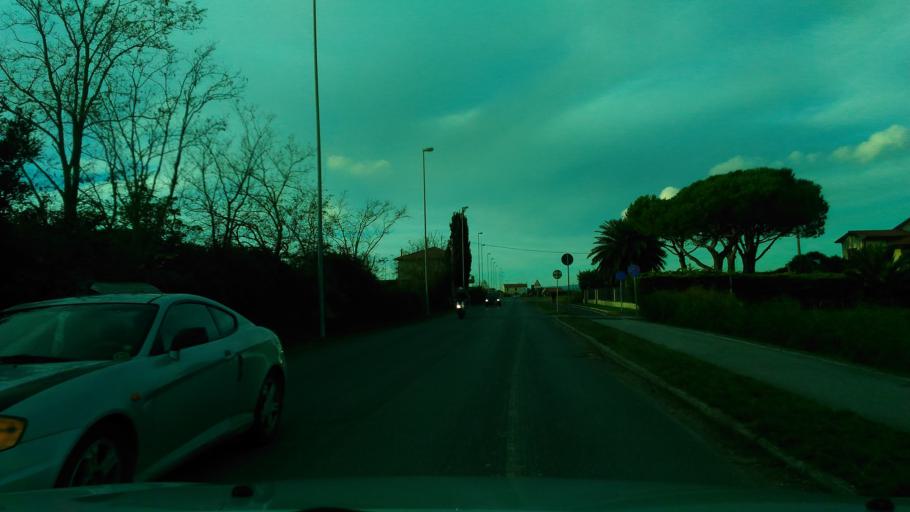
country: IT
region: Tuscany
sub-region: Provincia di Livorno
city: S.P. in Palazzi
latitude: 43.3081
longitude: 10.4896
